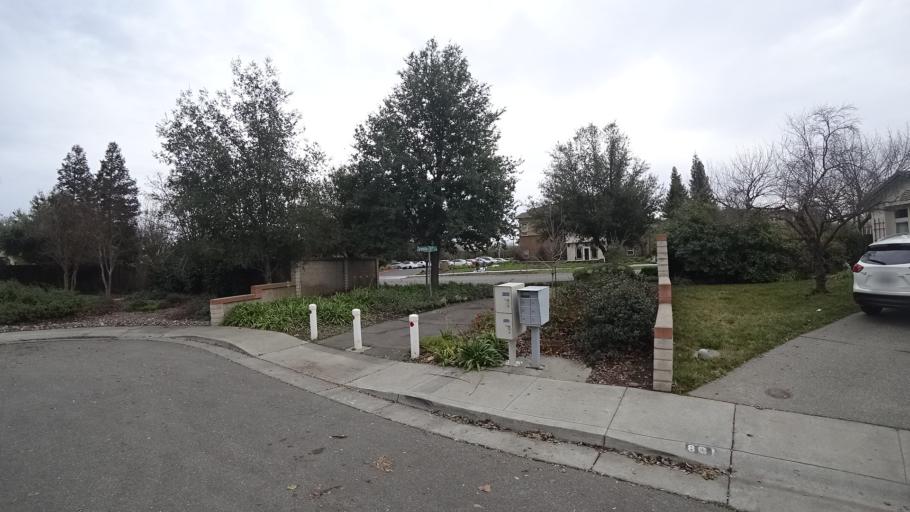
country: US
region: California
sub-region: Yolo County
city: Davis
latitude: 38.5524
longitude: -121.7181
